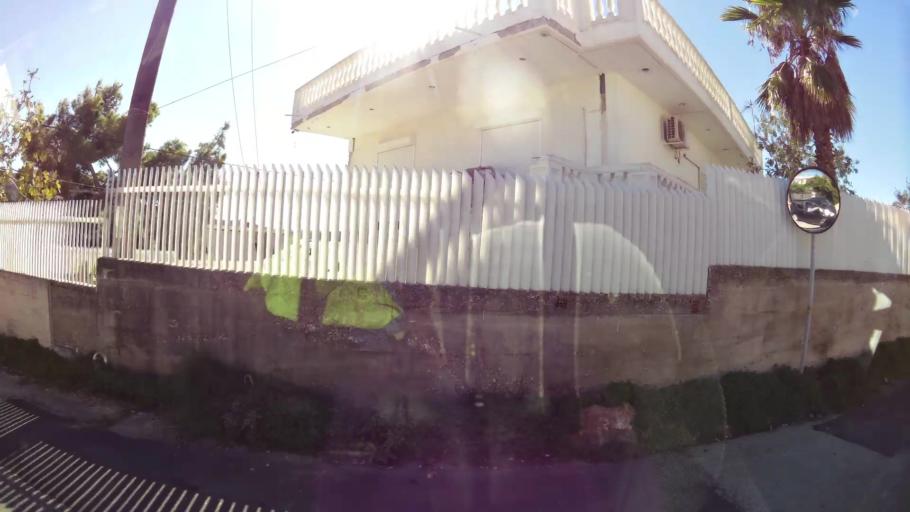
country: GR
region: Attica
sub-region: Nomarchia Anatolikis Attikis
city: Kitsi
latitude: 37.8476
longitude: 23.8237
